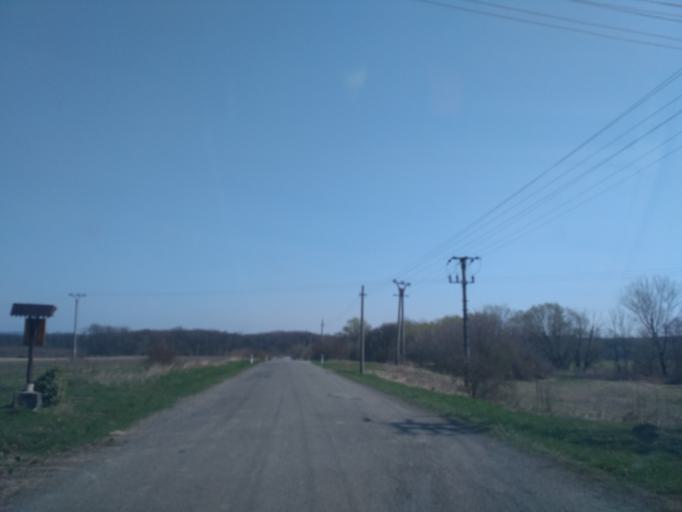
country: SK
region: Presovsky
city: Vranov nad Topl'ou
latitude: 48.8018
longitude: 21.6502
